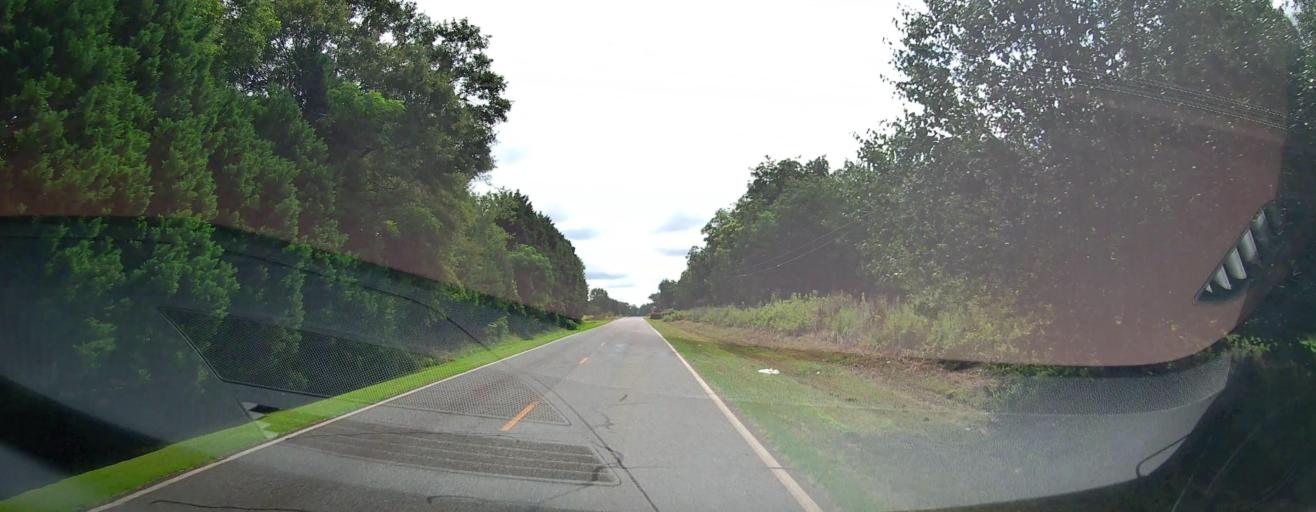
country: US
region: Georgia
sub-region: Peach County
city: Byron
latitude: 32.6450
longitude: -83.7839
